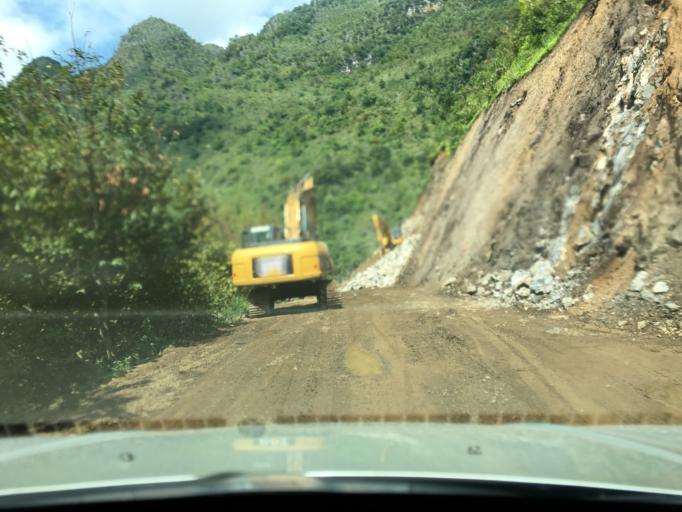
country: CN
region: Guizhou Sheng
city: Liupanshui
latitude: 25.9090
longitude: 105.1008
